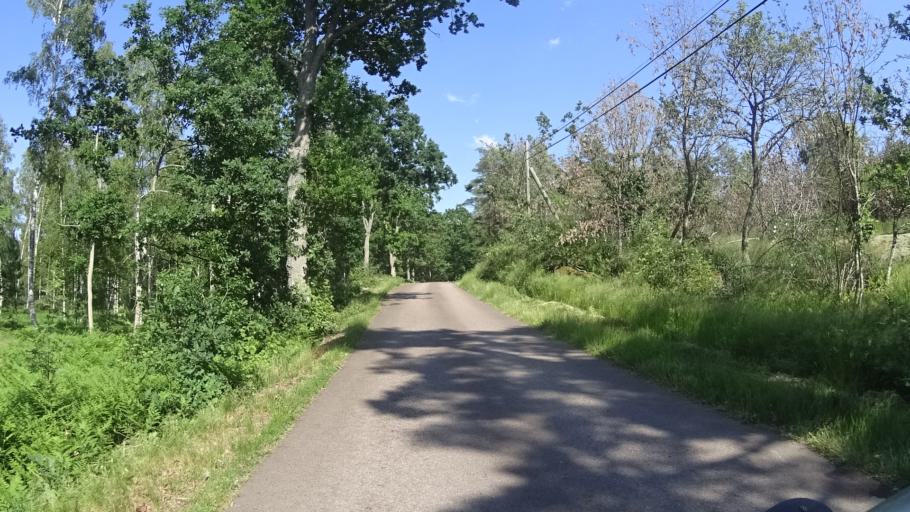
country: SE
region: Kalmar
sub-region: Oskarshamns Kommun
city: Oskarshamn
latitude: 57.2320
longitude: 16.4886
